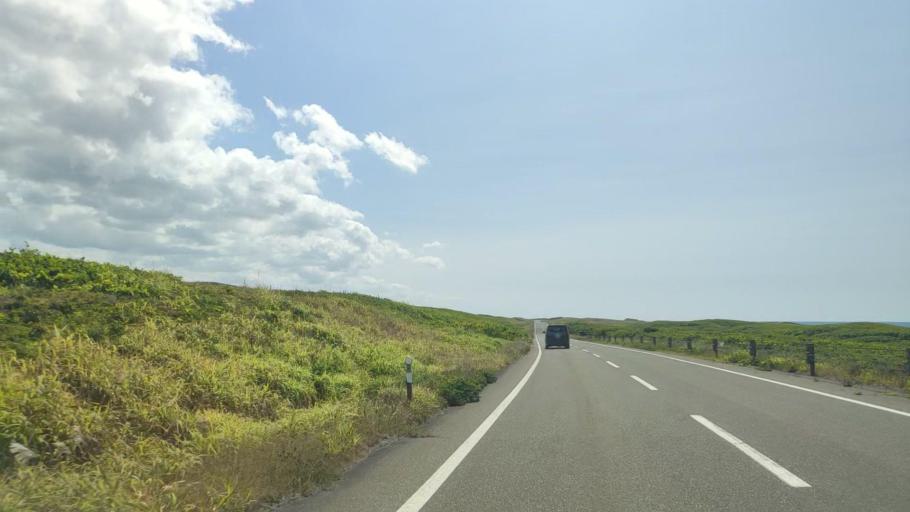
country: JP
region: Hokkaido
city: Wakkanai
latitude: 45.2053
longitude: 141.5711
